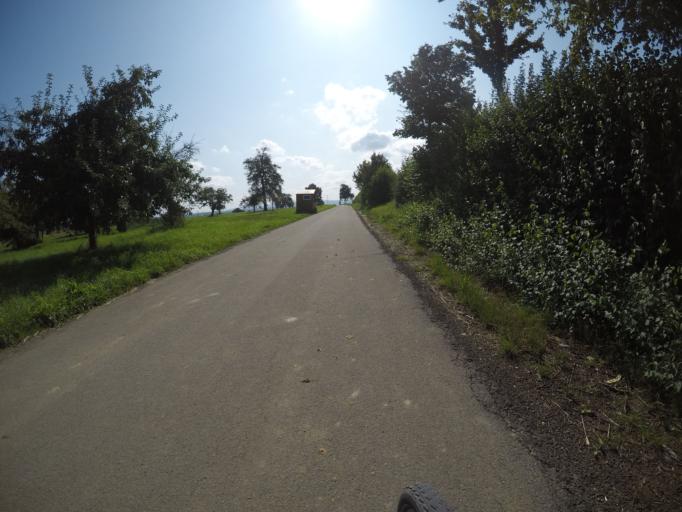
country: DE
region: Baden-Wuerttemberg
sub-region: Regierungsbezirk Stuttgart
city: Kongen
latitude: 48.6882
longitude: 9.3423
